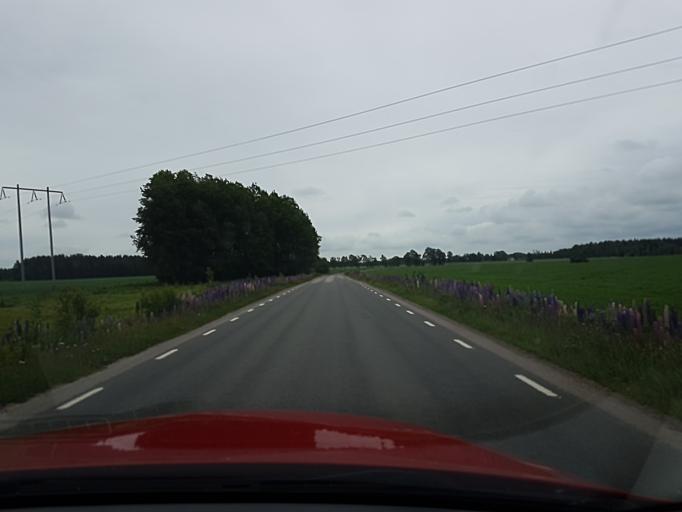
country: SE
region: Vaestra Goetaland
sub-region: Skovde Kommun
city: Skoevde
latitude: 58.3800
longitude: 13.9231
